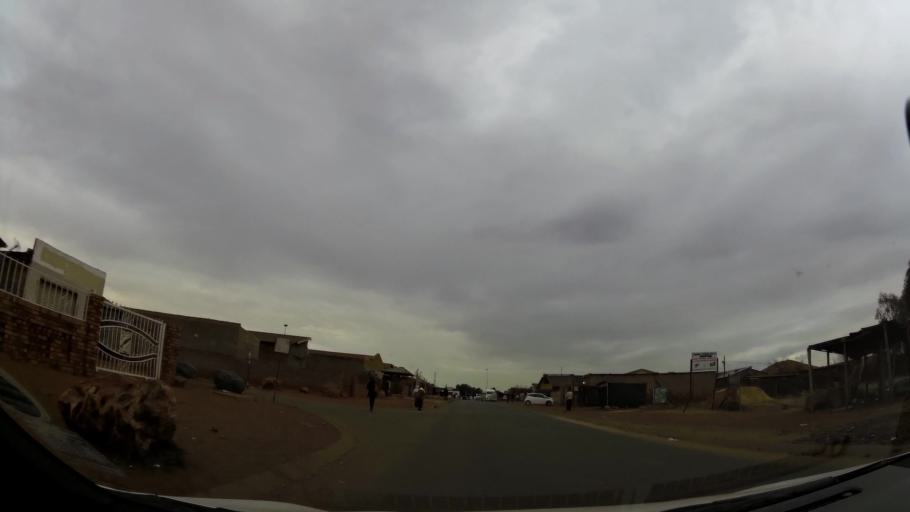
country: ZA
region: Gauteng
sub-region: Ekurhuleni Metropolitan Municipality
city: Germiston
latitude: -26.3760
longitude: 28.1601
